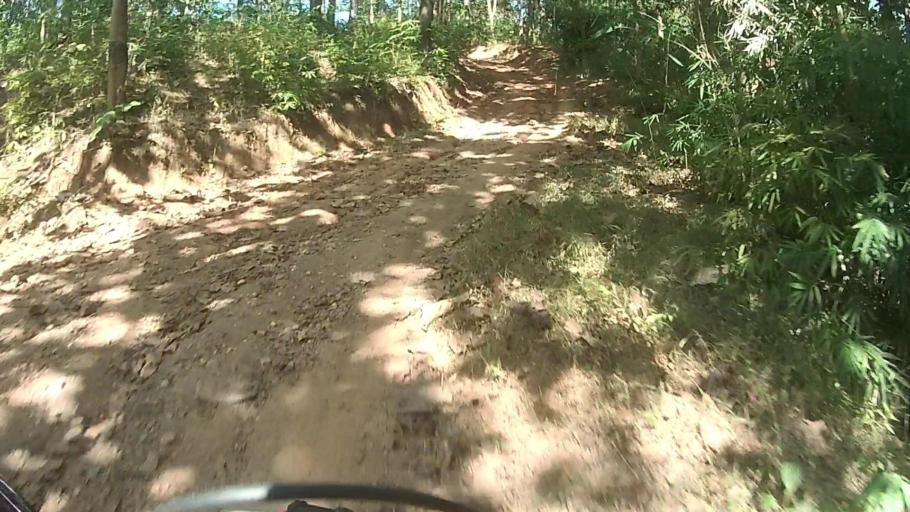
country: TH
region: Chiang Mai
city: Mae On
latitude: 19.0193
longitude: 99.3006
